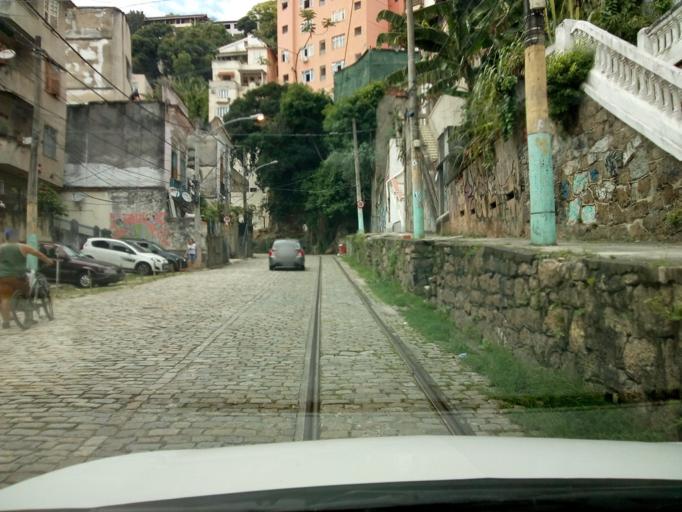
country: BR
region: Rio de Janeiro
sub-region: Rio De Janeiro
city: Rio de Janeiro
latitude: -22.9157
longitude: -43.1826
